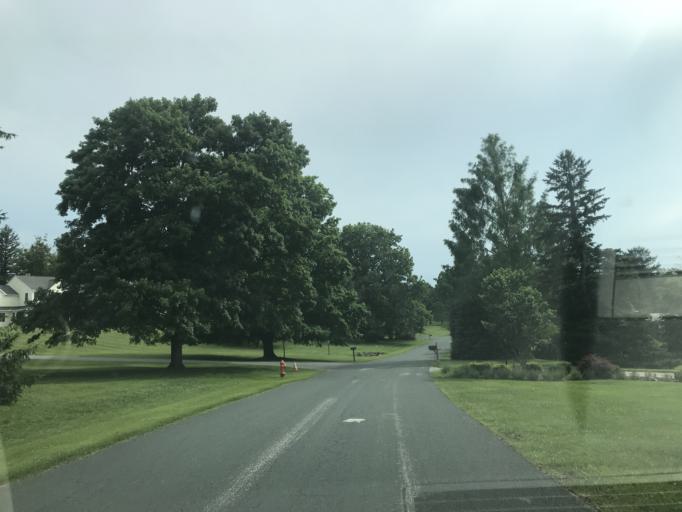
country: US
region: Maryland
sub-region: Baltimore County
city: Hampton
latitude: 39.4236
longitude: -76.5903
